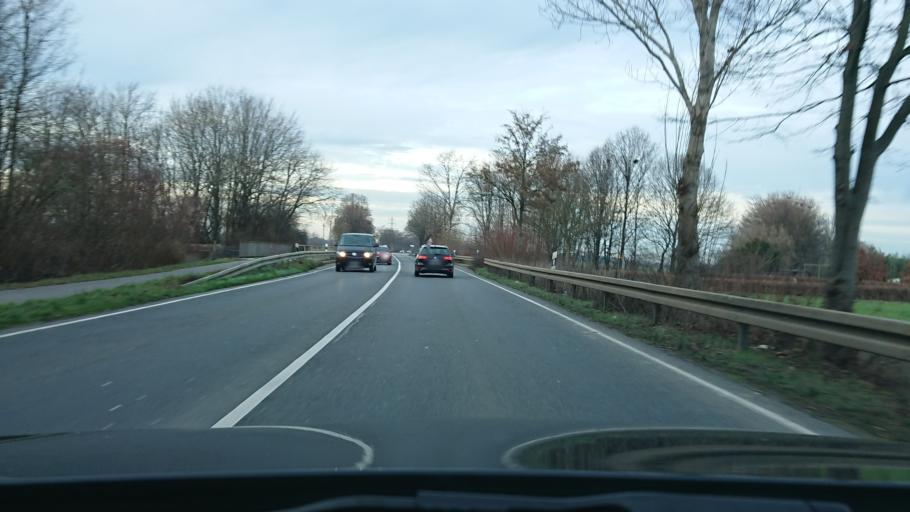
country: DE
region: North Rhine-Westphalia
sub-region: Regierungsbezirk Koln
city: Frechen
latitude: 50.9425
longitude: 6.8114
